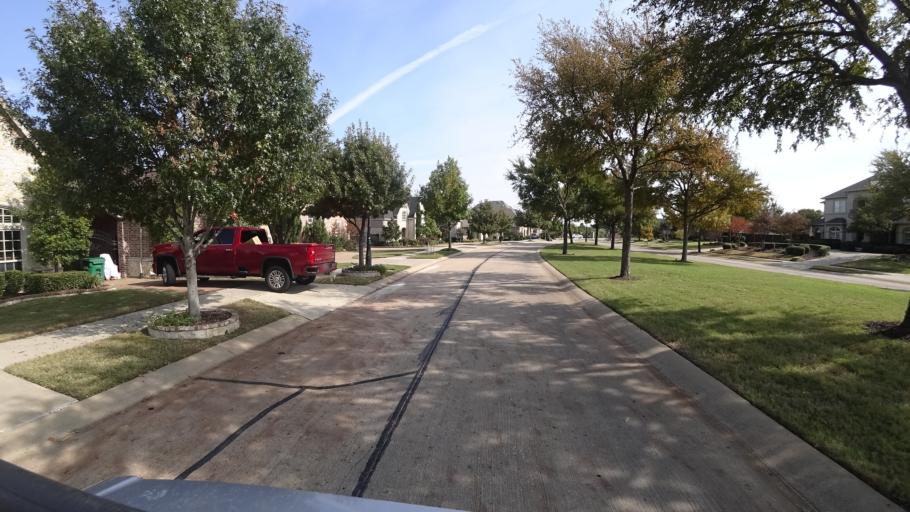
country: US
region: Texas
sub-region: Denton County
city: The Colony
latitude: 33.0368
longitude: -96.8905
